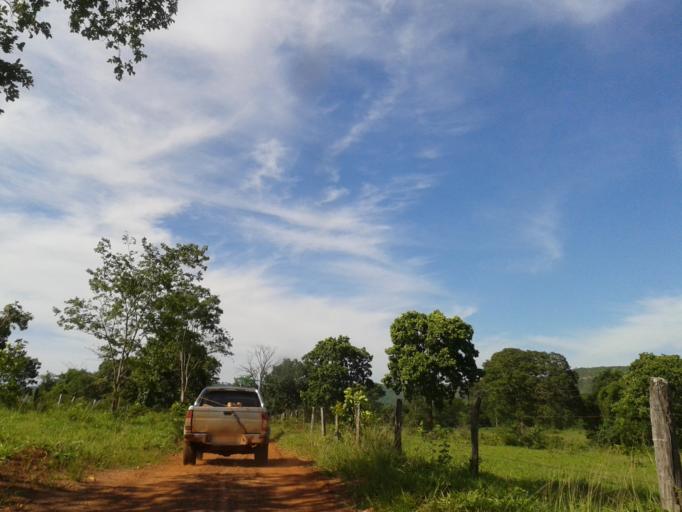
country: BR
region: Minas Gerais
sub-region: Santa Vitoria
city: Santa Vitoria
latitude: -19.0790
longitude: -50.0154
